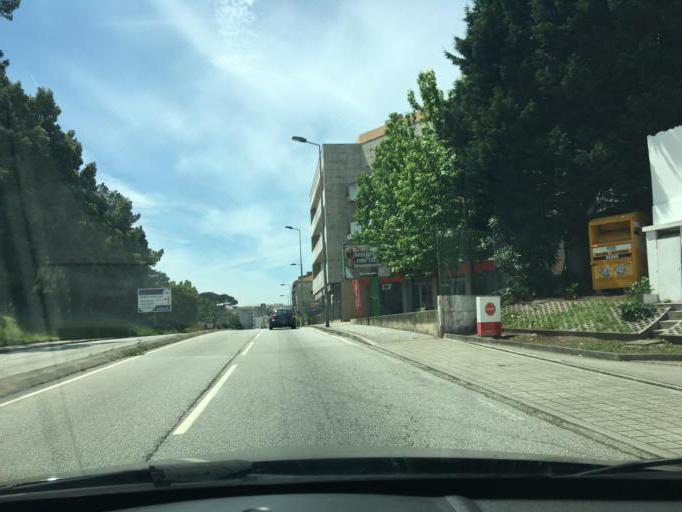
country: PT
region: Porto
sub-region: Porto
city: Porto
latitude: 41.1688
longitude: -8.6065
